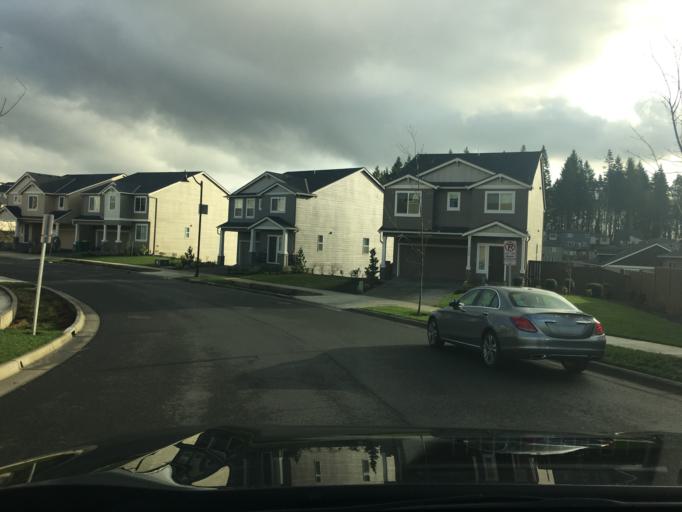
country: US
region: Oregon
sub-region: Washington County
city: Bethany
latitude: 45.5728
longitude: -122.8535
